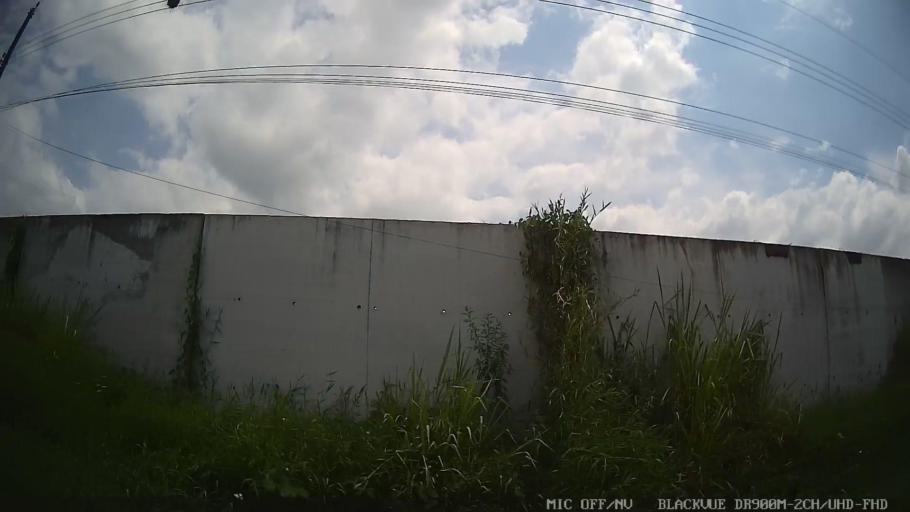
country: BR
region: Sao Paulo
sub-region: Caraguatatuba
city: Caraguatatuba
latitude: -23.6689
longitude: -45.4592
